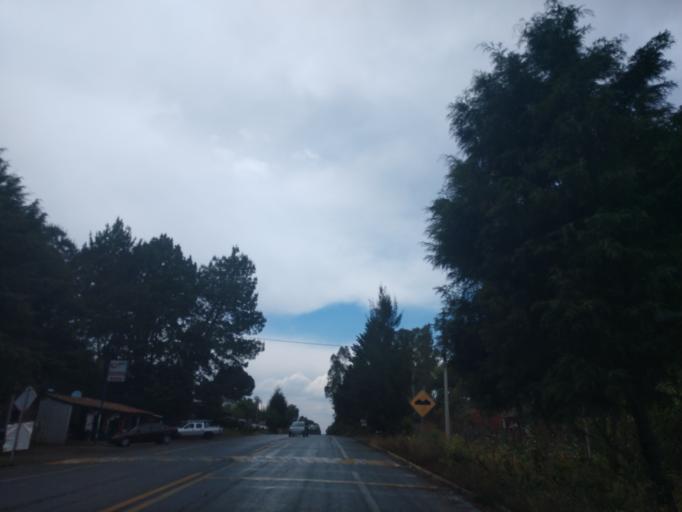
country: MX
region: Jalisco
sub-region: Mazamitla
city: Mazamitla
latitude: 19.9463
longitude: -103.0680
